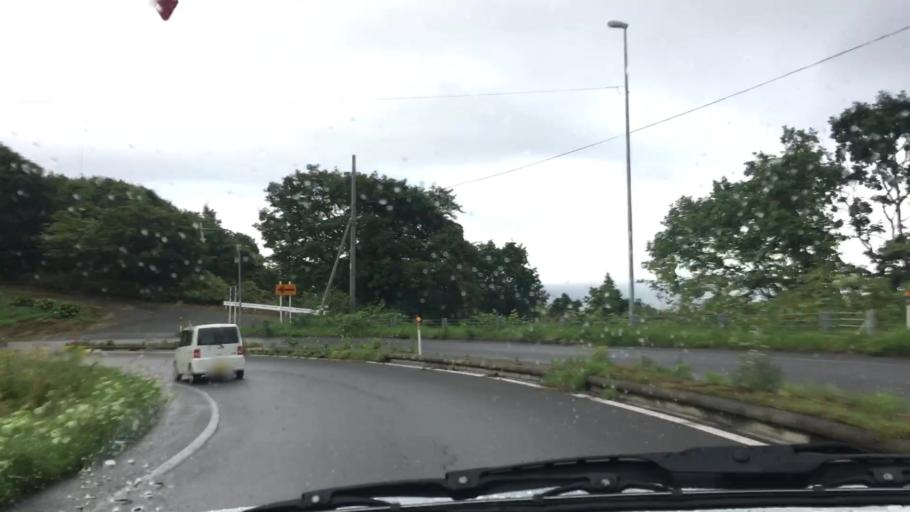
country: JP
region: Hokkaido
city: Date
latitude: 42.5915
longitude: 140.7208
